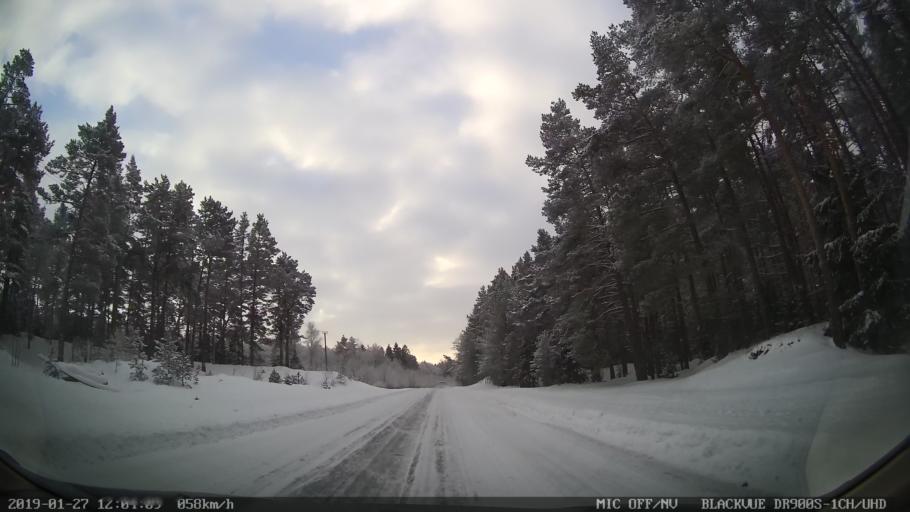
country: EE
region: Harju
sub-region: Raasiku vald
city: Raasiku
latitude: 59.4854
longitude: 25.2601
